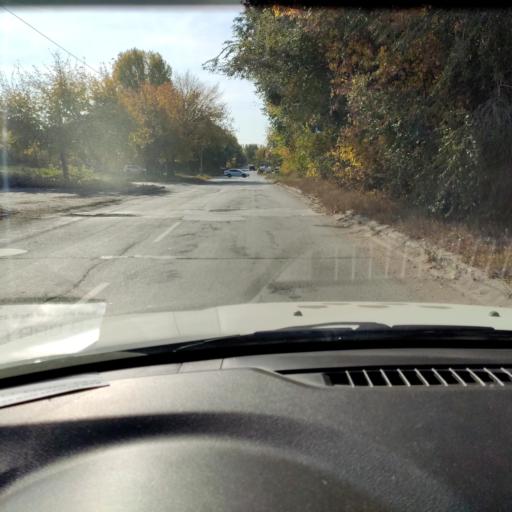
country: RU
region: Samara
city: Tol'yatti
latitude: 53.5564
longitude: 49.3096
